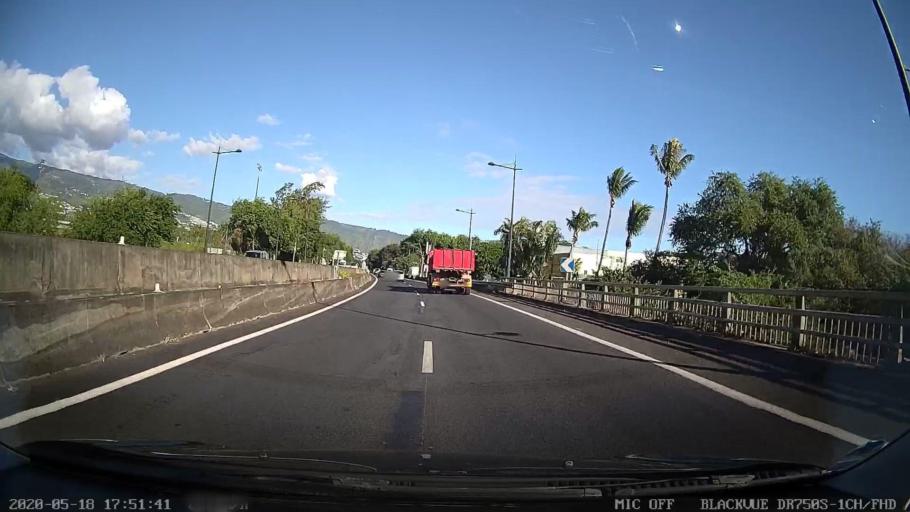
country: RE
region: Reunion
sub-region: Reunion
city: Saint-Denis
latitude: -20.8853
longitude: 55.4971
